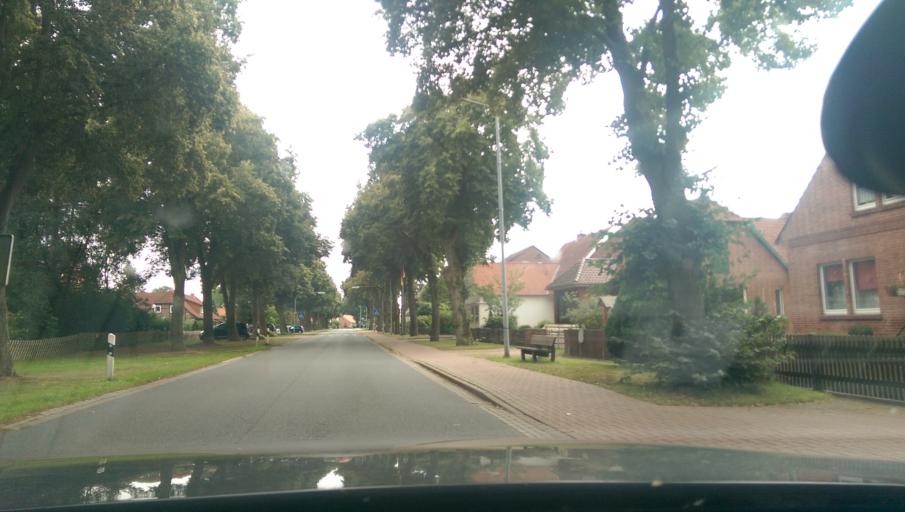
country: DE
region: Lower Saxony
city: Frankenfeld
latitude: 52.6963
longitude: 9.4805
